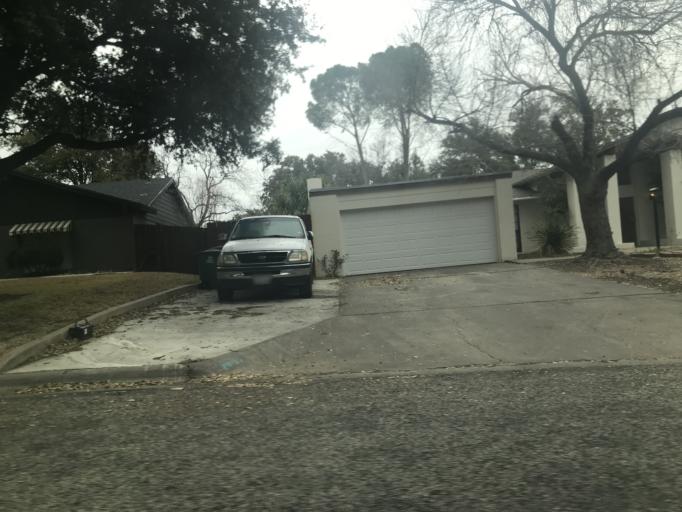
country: US
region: Texas
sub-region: Tom Green County
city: San Angelo
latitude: 31.4238
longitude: -100.4759
